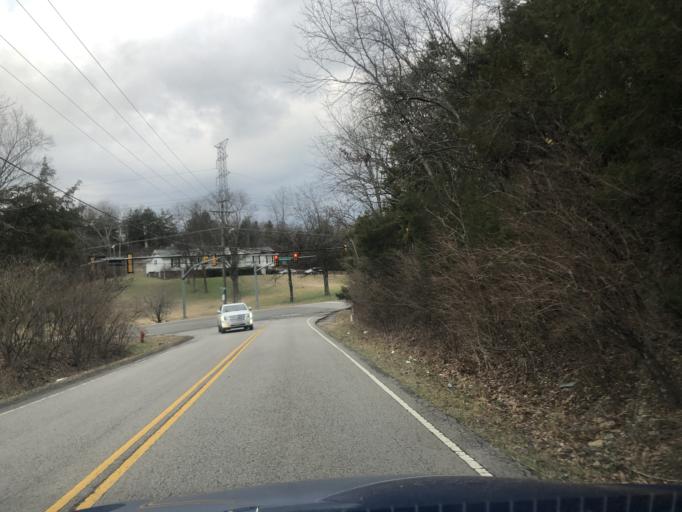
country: US
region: Tennessee
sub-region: Davidson County
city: Belle Meade
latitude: 36.1117
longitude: -86.9294
